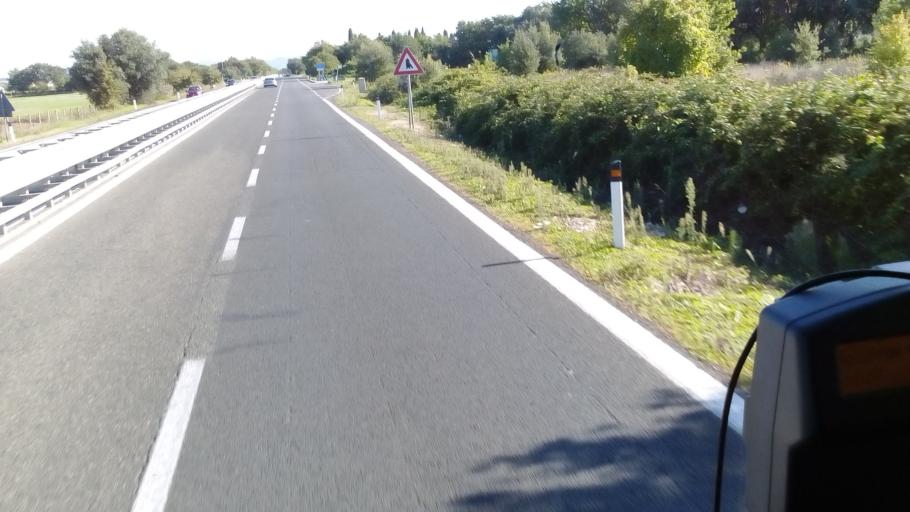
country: IT
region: Latium
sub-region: Provincia di Viterbo
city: Tarquinia
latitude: 42.2939
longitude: 11.6791
